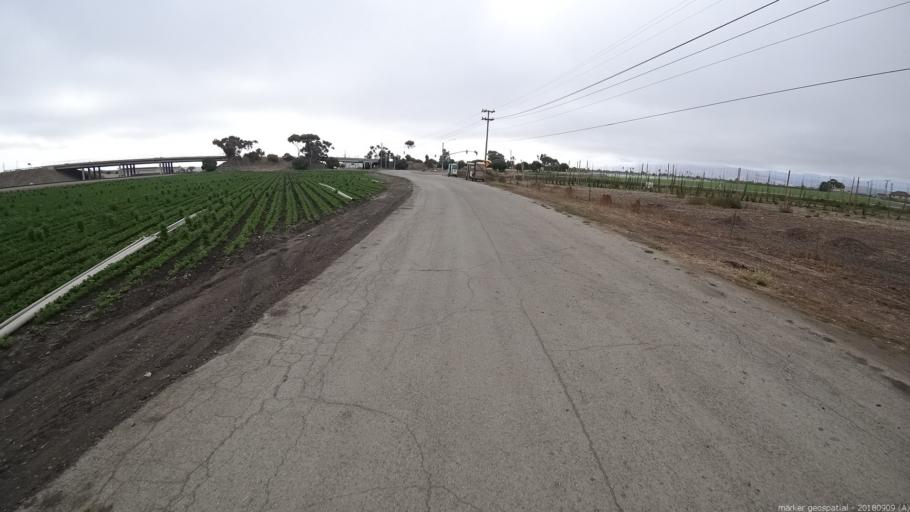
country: US
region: California
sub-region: Monterey County
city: Boronda
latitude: 36.6859
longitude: -121.6771
